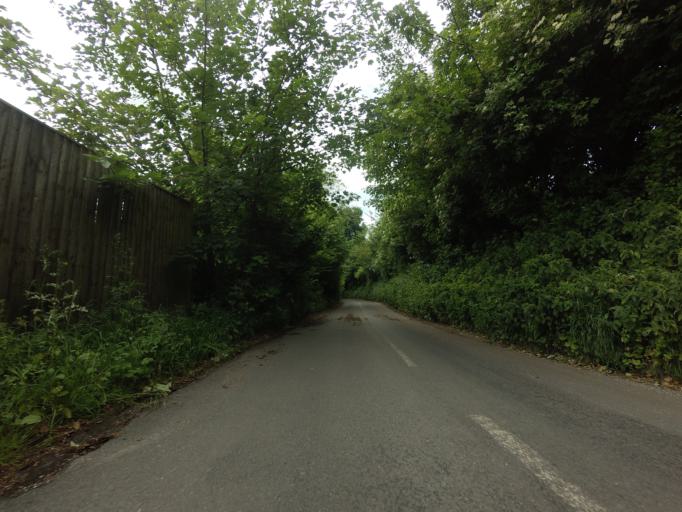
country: GB
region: England
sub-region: Kent
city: Shoreham
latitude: 51.3395
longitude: 0.1774
